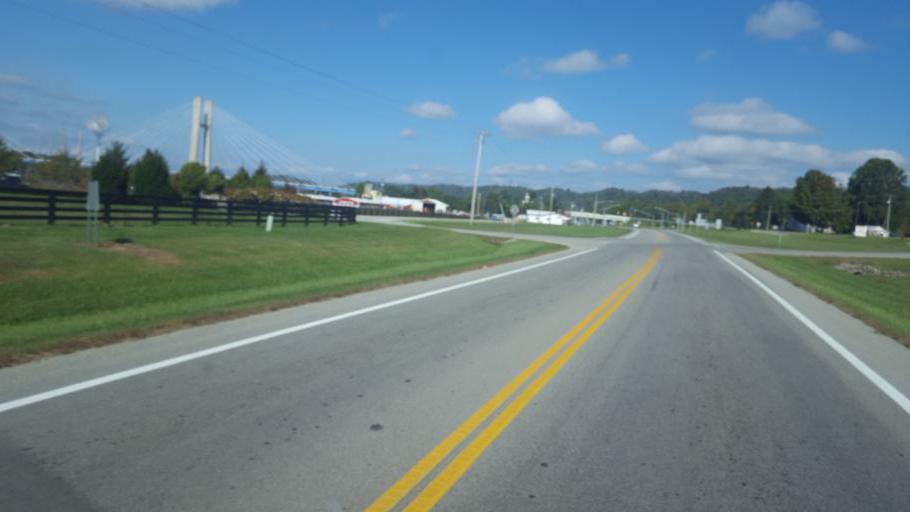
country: US
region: Ohio
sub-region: Brown County
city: Aberdeen
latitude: 38.6813
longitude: -83.7744
